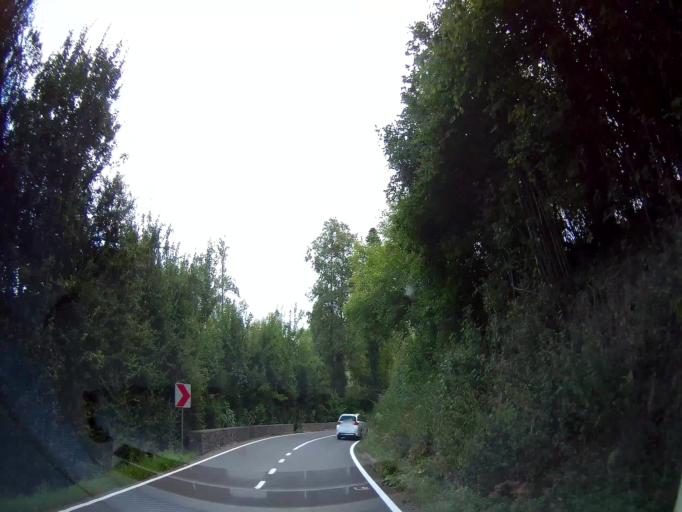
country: BE
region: Wallonia
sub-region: Province de Namur
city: Onhaye
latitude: 50.2924
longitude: 4.8142
